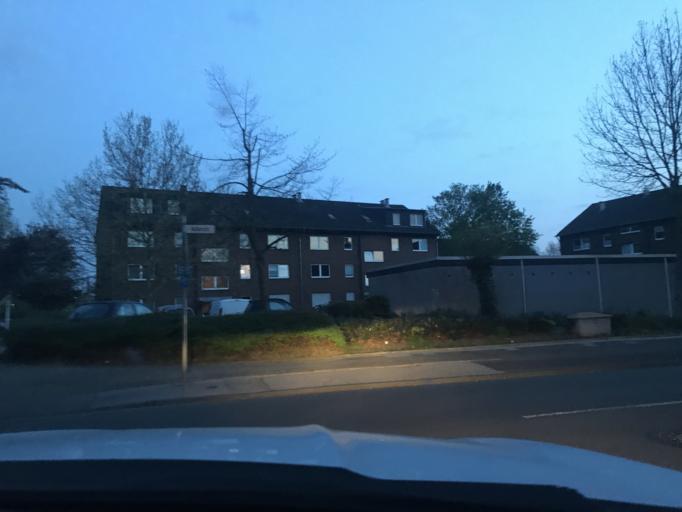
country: DE
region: North Rhine-Westphalia
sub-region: Regierungsbezirk Dusseldorf
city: Hochfeld
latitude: 51.3840
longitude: 6.7067
